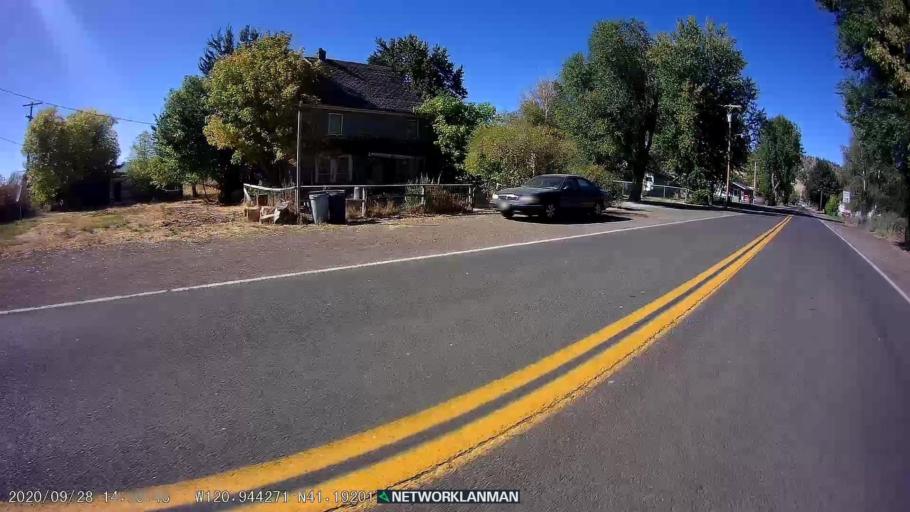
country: US
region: California
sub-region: Modoc County
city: Alturas
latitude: 41.1923
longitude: -120.9443
